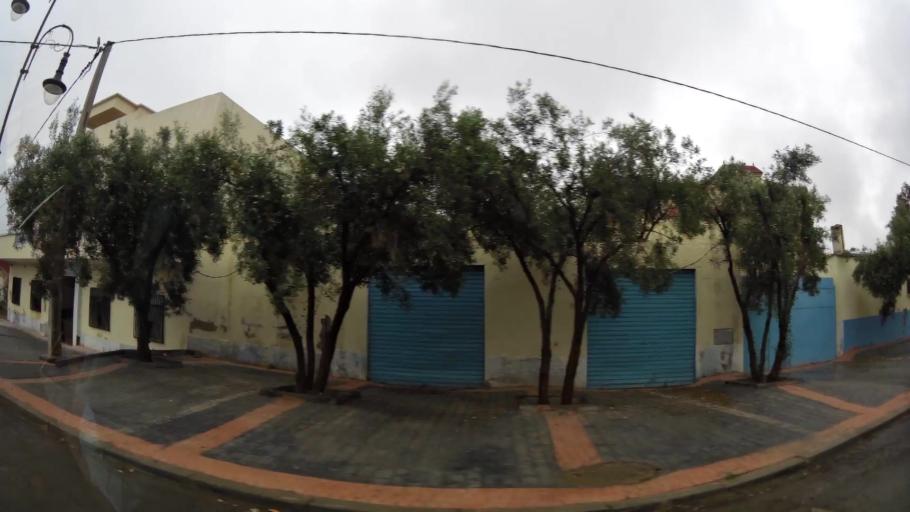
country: MA
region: Taza-Al Hoceima-Taounate
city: Imzourene
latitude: 35.1776
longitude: -3.8791
